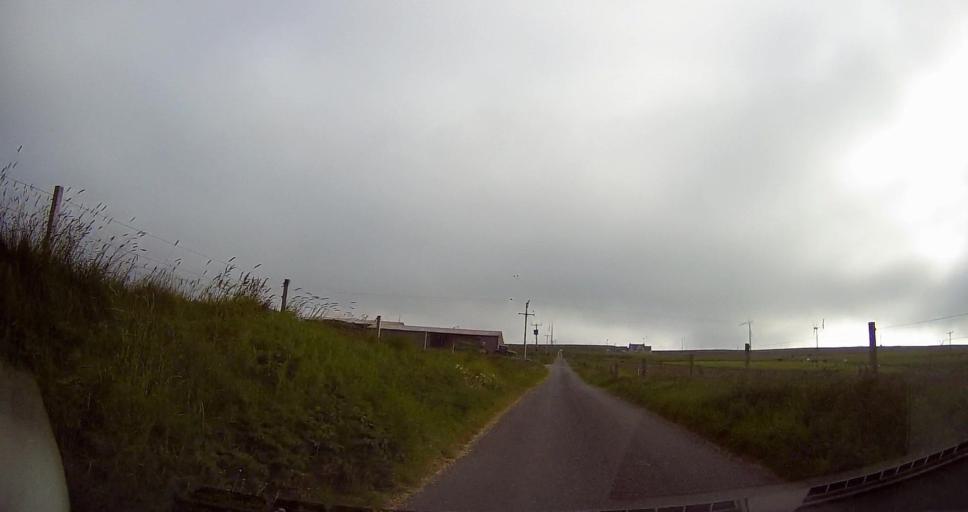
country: GB
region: Scotland
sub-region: Orkney Islands
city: Orkney
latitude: 59.1198
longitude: -3.1267
